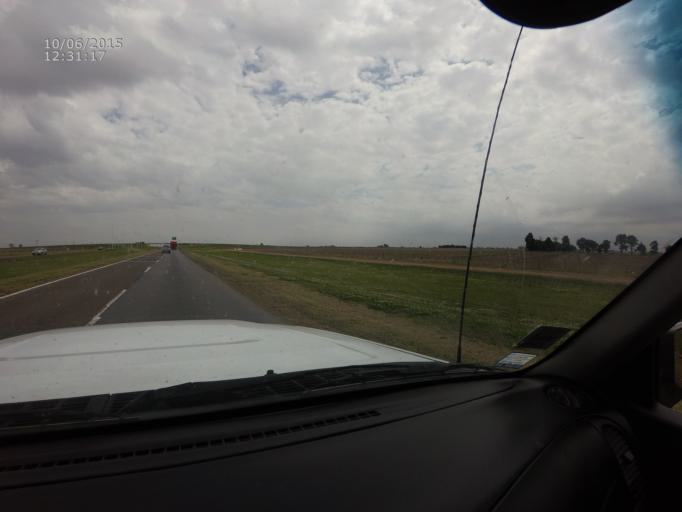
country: AR
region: Santa Fe
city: Carcarana
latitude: -32.8851
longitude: -61.1209
